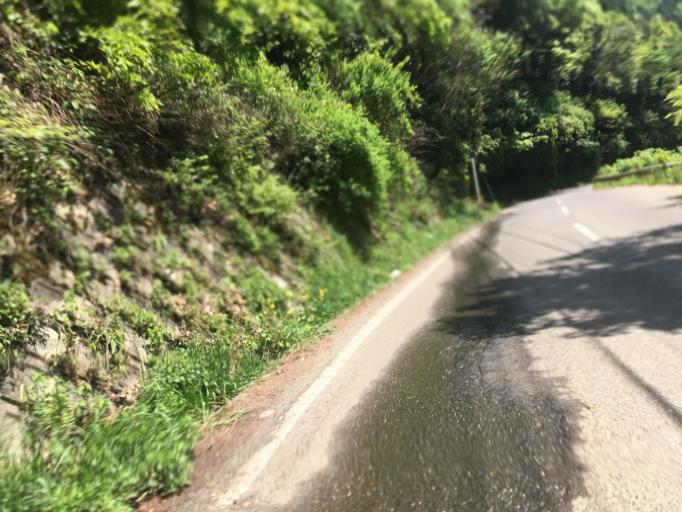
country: JP
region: Kyoto
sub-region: Kyoto-shi
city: Kamigyo-ku
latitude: 35.0873
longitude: 135.7412
